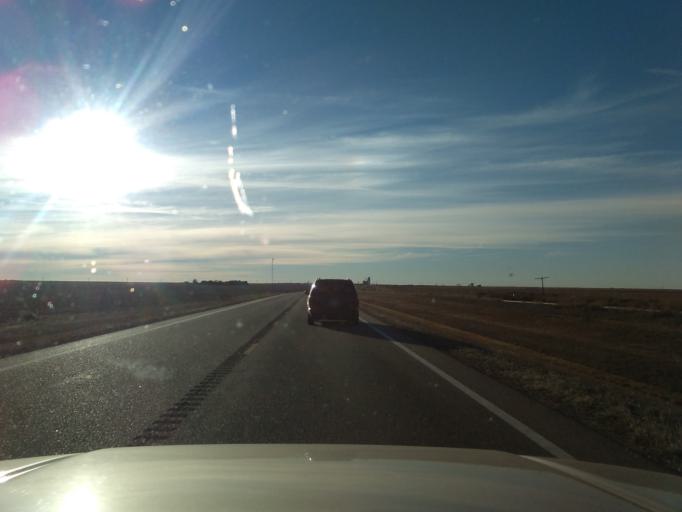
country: US
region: Kansas
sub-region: Thomas County
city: Colby
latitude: 39.4587
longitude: -100.7809
